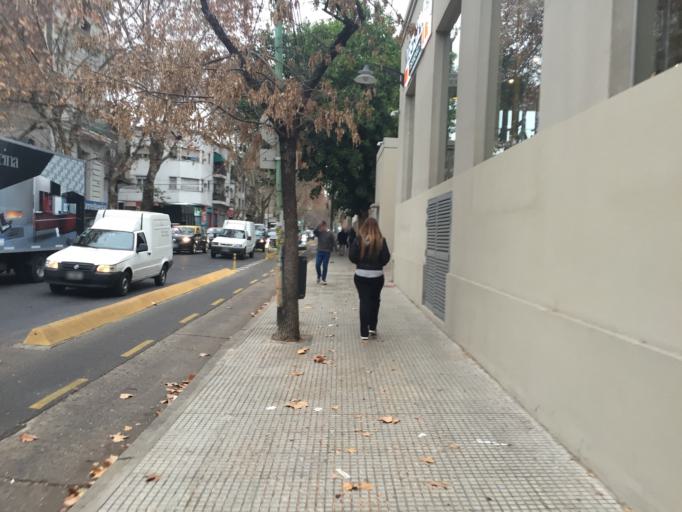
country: AR
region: Buenos Aires F.D.
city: Colegiales
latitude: -34.5793
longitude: -58.4257
